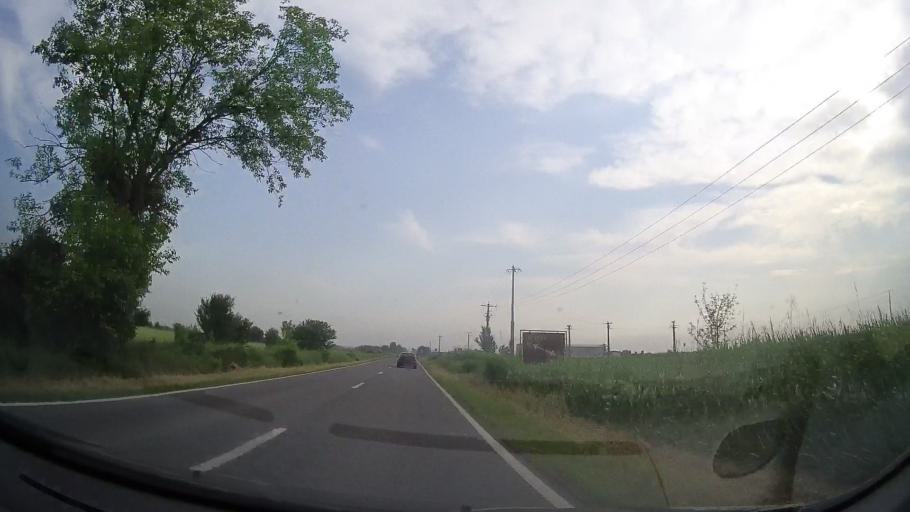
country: RO
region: Timis
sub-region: Comuna Sag
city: Sag
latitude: 45.6825
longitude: 21.1674
